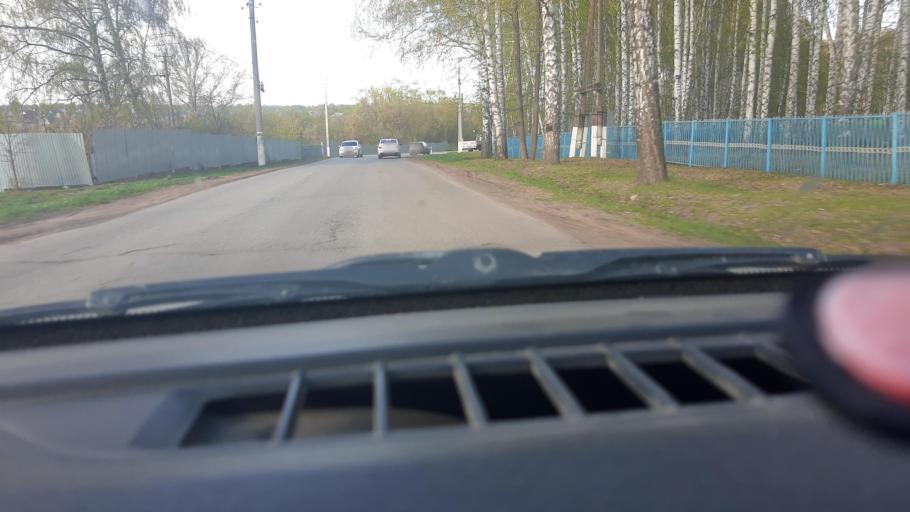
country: RU
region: Bashkortostan
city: Chishmy
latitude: 54.5975
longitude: 55.3710
